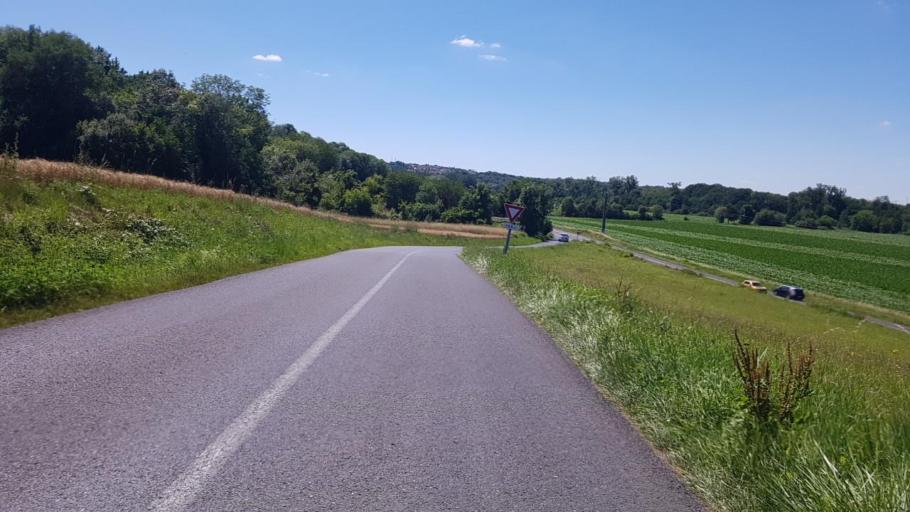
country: FR
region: Ile-de-France
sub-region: Departement de Seine-et-Marne
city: Fublaines
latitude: 48.9392
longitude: 2.9241
